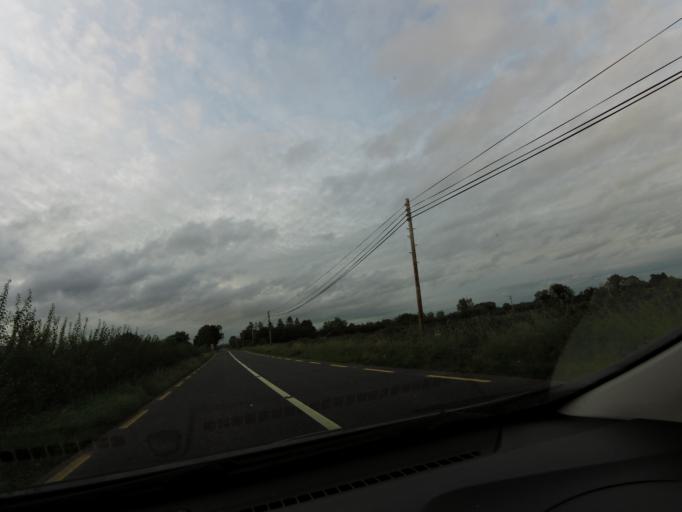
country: IE
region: Leinster
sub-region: Uibh Fhaili
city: Ferbane
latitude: 53.3629
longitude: -7.8527
